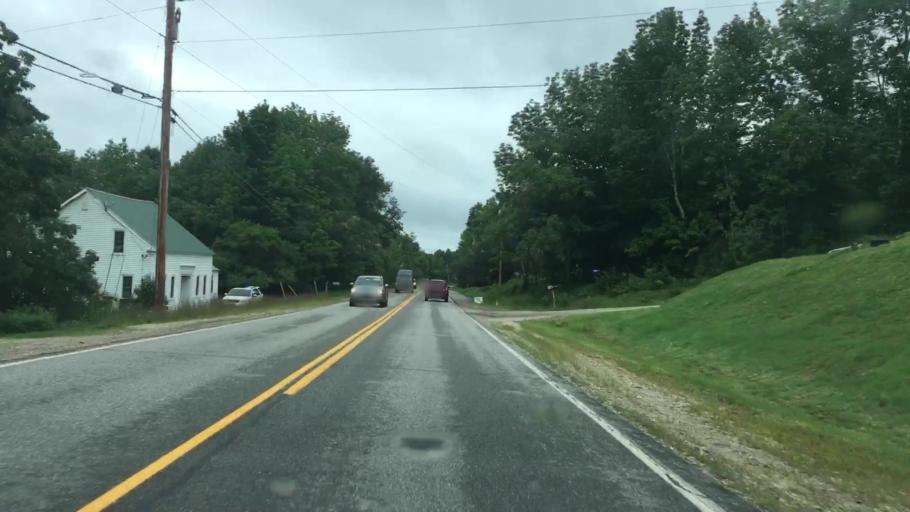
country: US
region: Maine
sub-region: Oxford County
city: Brownfield
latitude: 43.9623
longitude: -70.9043
